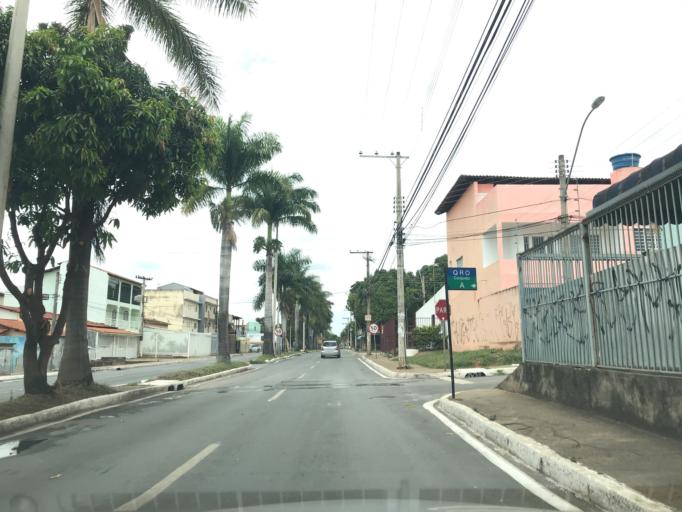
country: BR
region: Federal District
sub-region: Brasilia
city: Brasilia
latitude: -15.8533
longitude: -47.9483
